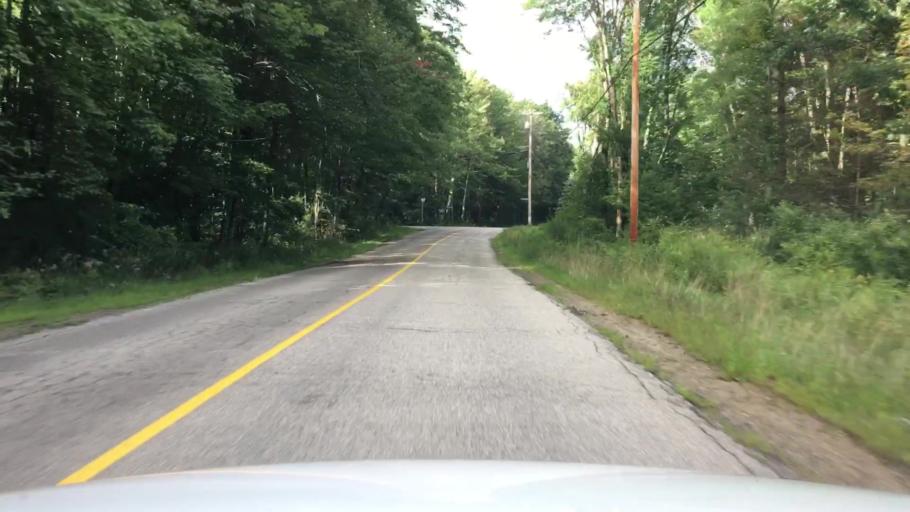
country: US
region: Maine
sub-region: York County
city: West Kennebunk
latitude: 43.4196
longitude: -70.6570
